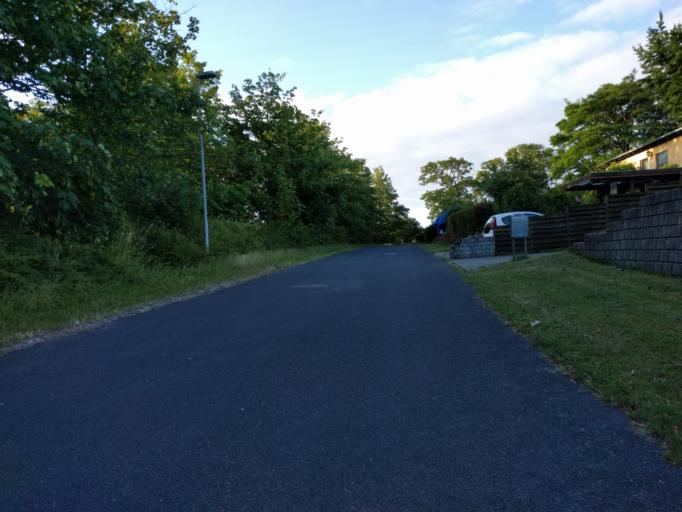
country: DK
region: South Denmark
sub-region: Kerteminde Kommune
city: Munkebo
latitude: 55.4563
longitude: 10.5524
